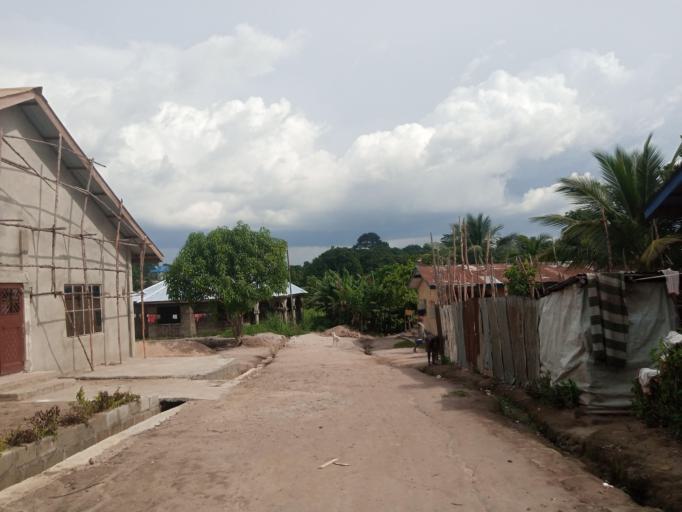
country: SL
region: Southern Province
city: Bo
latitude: 7.9811
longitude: -11.7405
